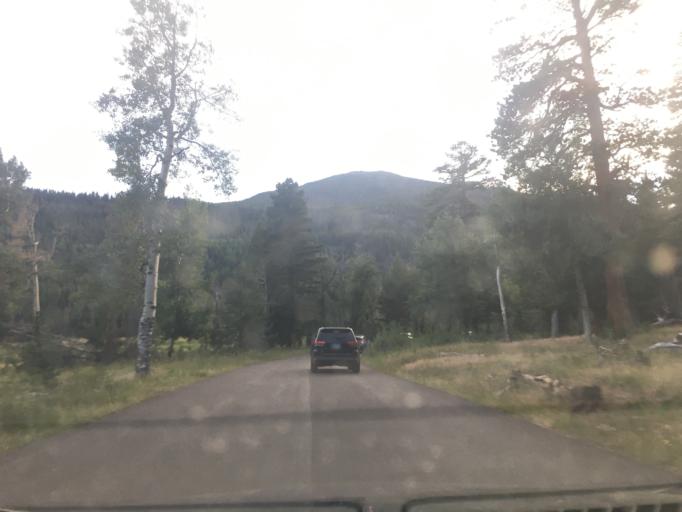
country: US
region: Colorado
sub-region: Larimer County
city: Estes Park
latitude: 40.4103
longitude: -105.6380
